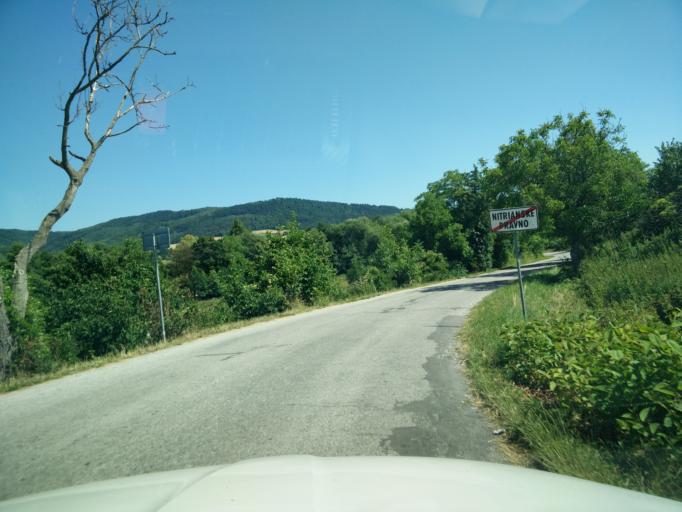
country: SK
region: Nitriansky
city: Prievidza
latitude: 48.8677
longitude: 18.6397
